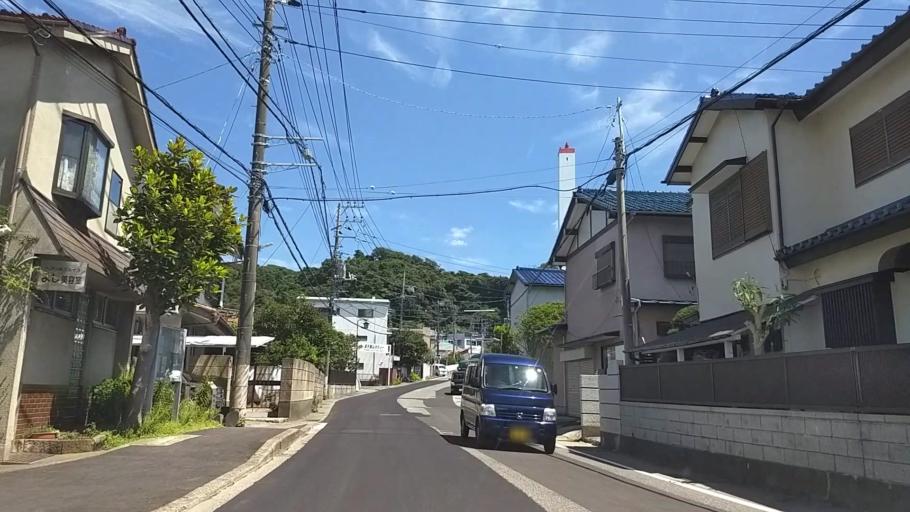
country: JP
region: Kanagawa
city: Kamakura
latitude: 35.3097
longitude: 139.5589
